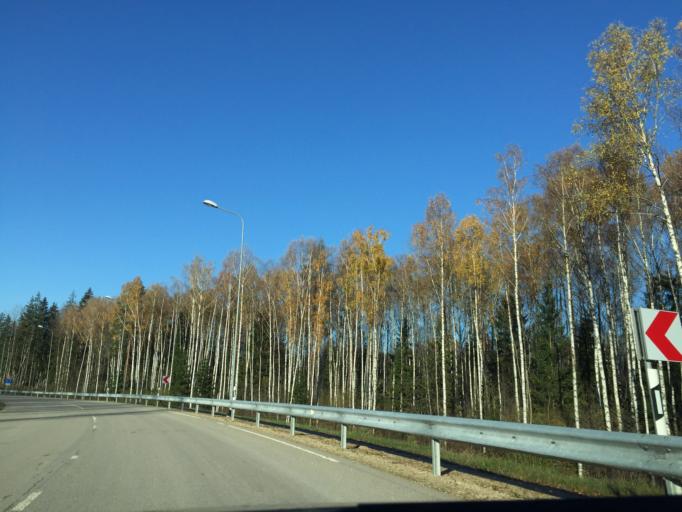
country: LV
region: Aizkraukles Rajons
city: Aizkraukle
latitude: 56.7043
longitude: 25.2818
